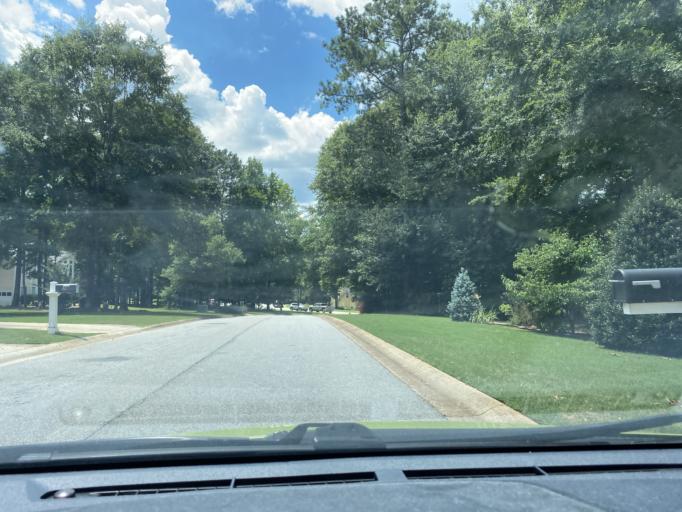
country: US
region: Georgia
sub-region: Fulton County
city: Palmetto
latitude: 33.4326
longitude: -84.6836
